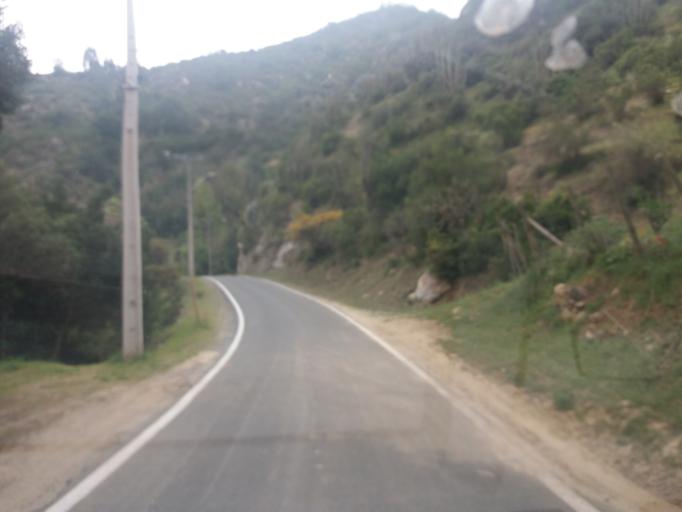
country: CL
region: Valparaiso
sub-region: Provincia de Marga Marga
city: Limache
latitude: -33.0330
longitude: -71.0861
